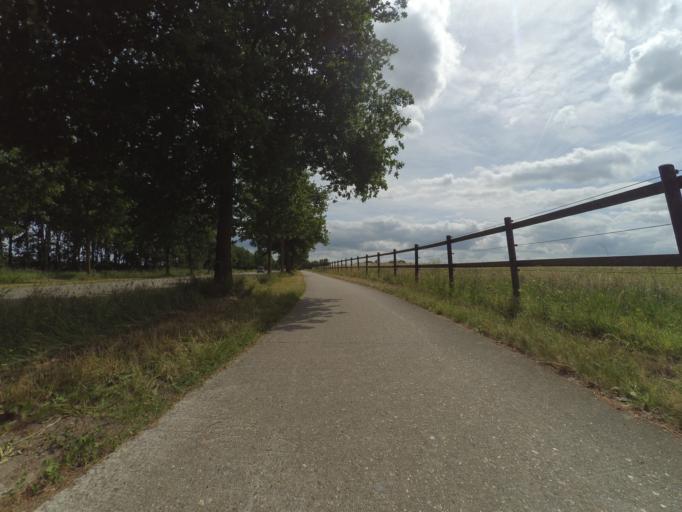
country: BE
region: Flanders
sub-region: Provincie Antwerpen
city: Essen
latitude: 51.4945
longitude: 4.3984
